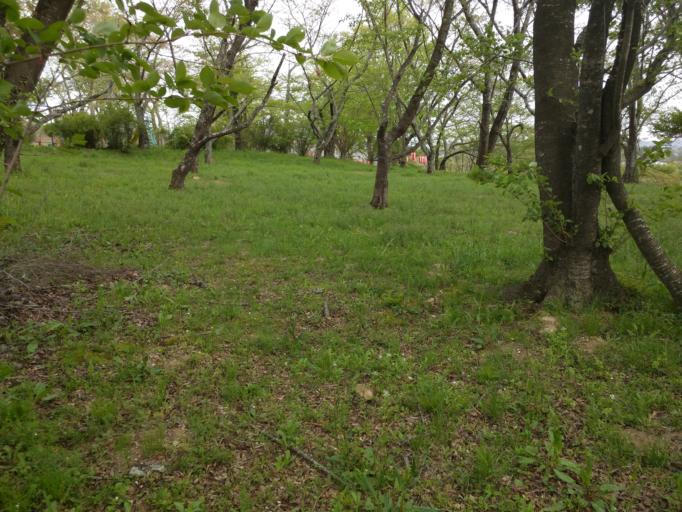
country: JP
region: Fukushima
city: Nihommatsu
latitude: 37.5643
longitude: 140.5117
